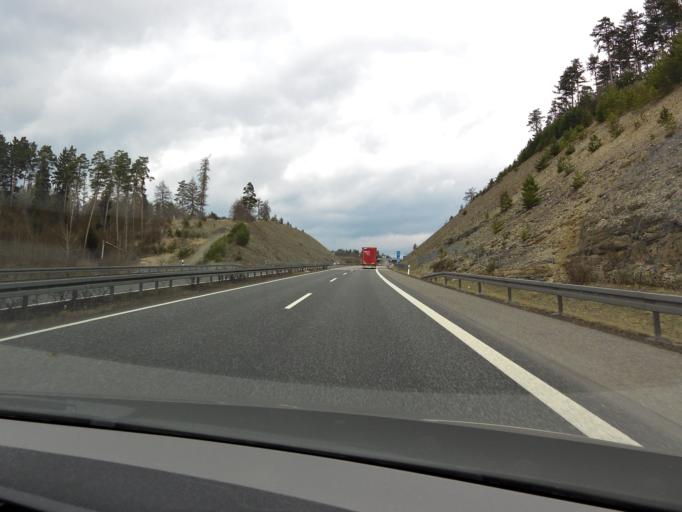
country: DE
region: Thuringia
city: Rohr
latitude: 50.5736
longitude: 10.4805
